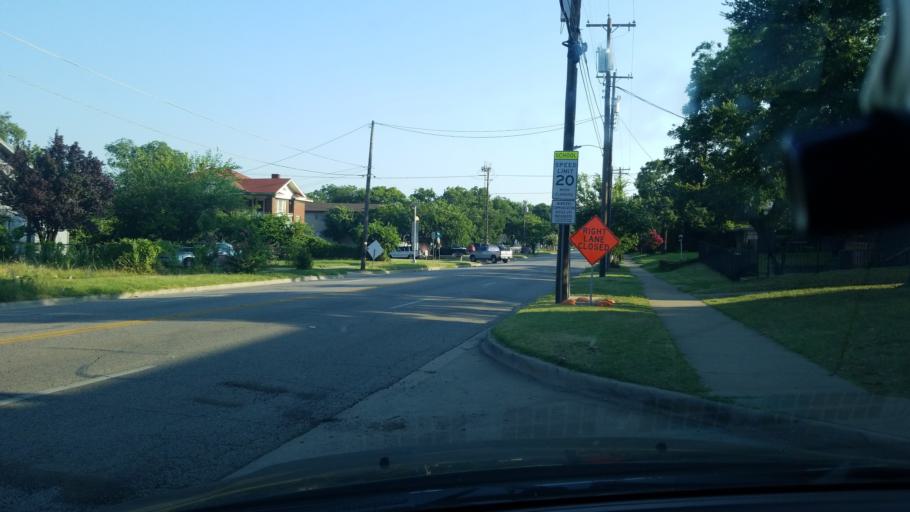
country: US
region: Texas
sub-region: Dallas County
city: Dallas
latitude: 32.7530
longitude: -96.8156
